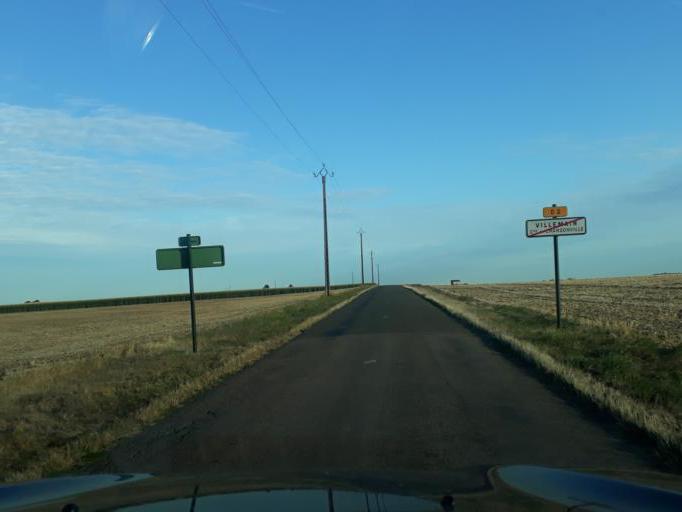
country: FR
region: Centre
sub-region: Departement du Loiret
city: Epieds-en-Beauce
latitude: 47.9454
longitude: 1.5704
